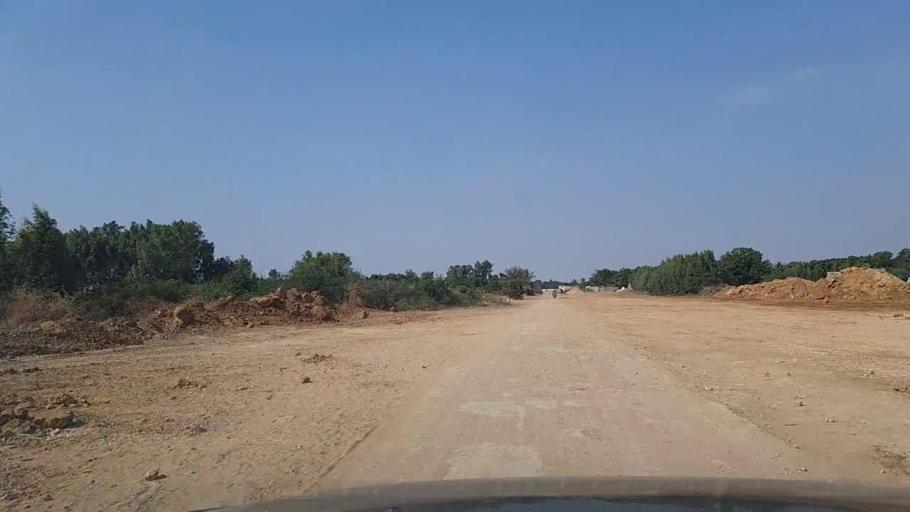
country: PK
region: Sindh
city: Gharo
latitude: 24.7627
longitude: 67.5781
